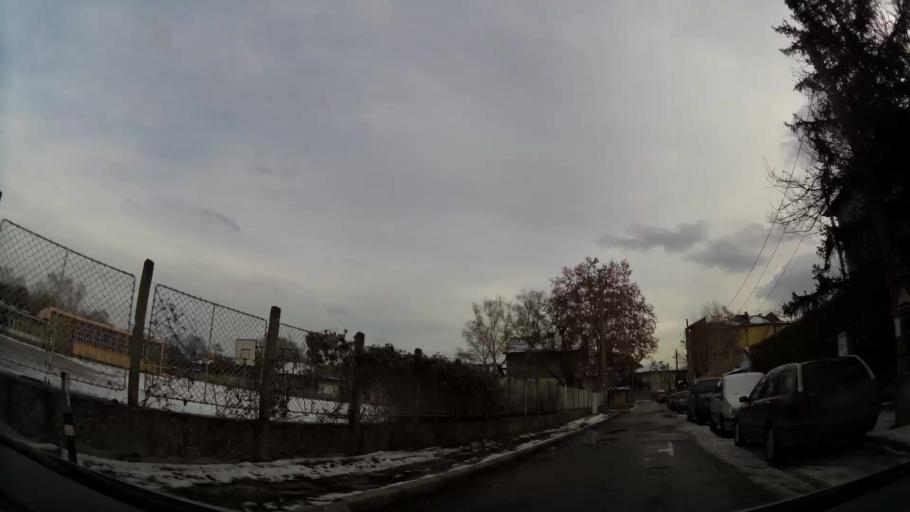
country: BG
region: Sofia-Capital
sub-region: Stolichna Obshtina
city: Sofia
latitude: 42.7248
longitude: 23.3385
